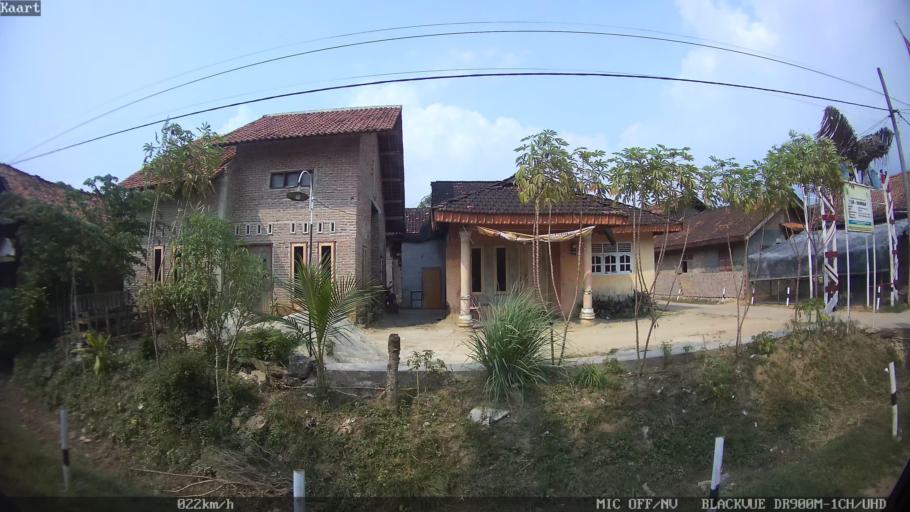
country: ID
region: Lampung
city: Kedondong
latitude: -5.4097
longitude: 105.0094
